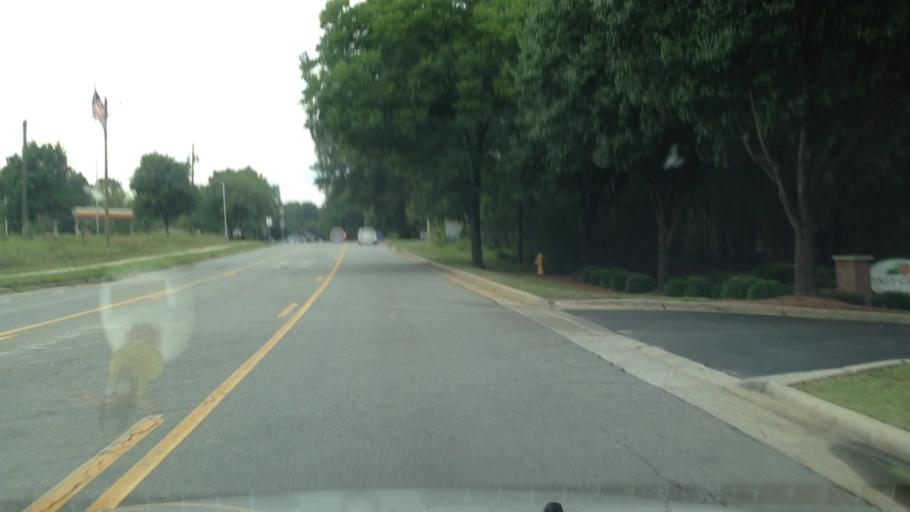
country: US
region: North Carolina
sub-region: Forsyth County
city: Kernersville
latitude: 36.1368
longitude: -80.0702
